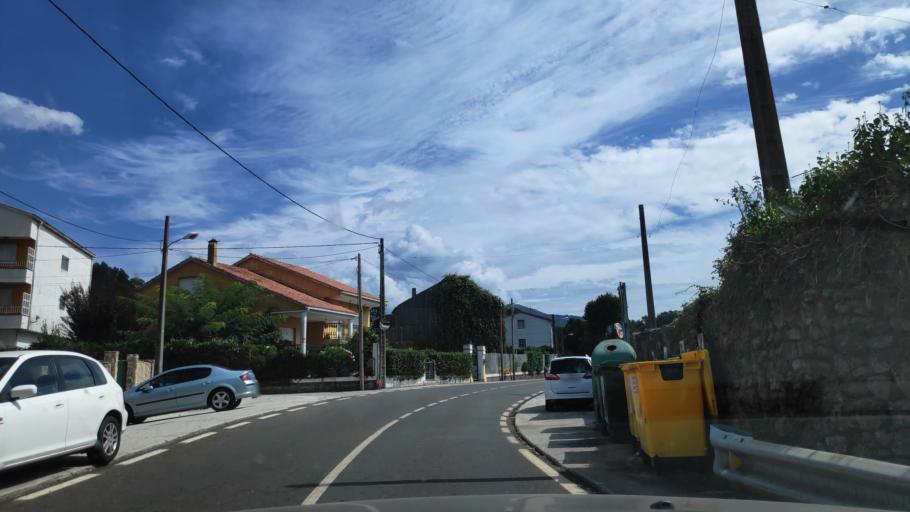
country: ES
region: Galicia
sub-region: Provincia da Coruna
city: Padron
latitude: 42.7327
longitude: -8.6685
